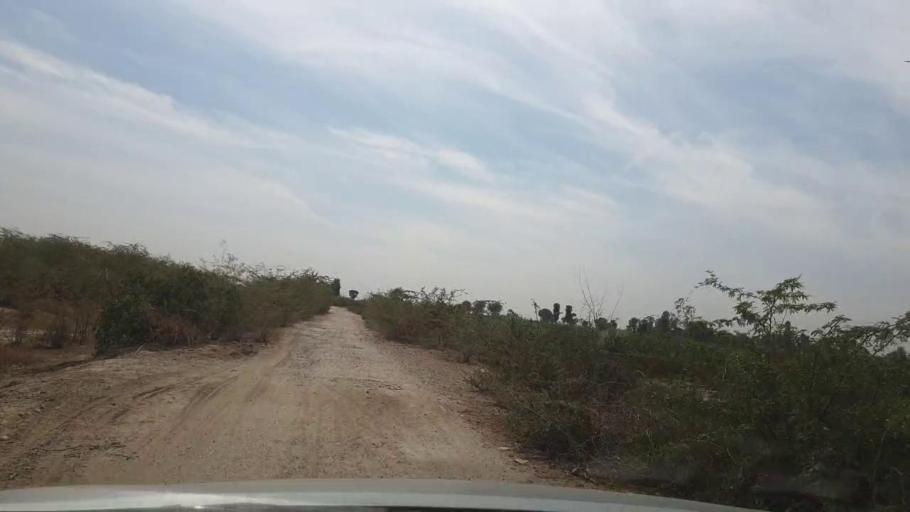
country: PK
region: Sindh
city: Nabisar
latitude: 25.0752
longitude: 69.5988
